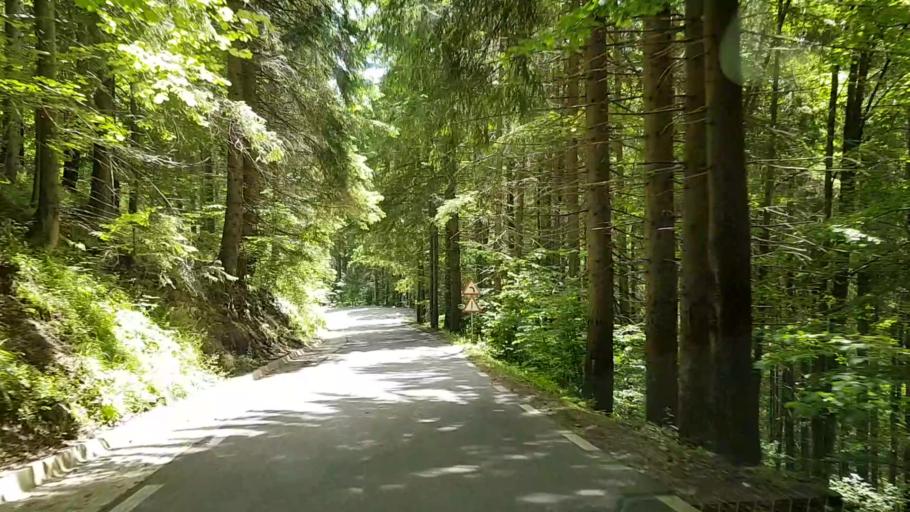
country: RO
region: Suceava
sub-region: Comuna Crucea
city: Crucea
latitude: 47.4234
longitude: 25.5759
